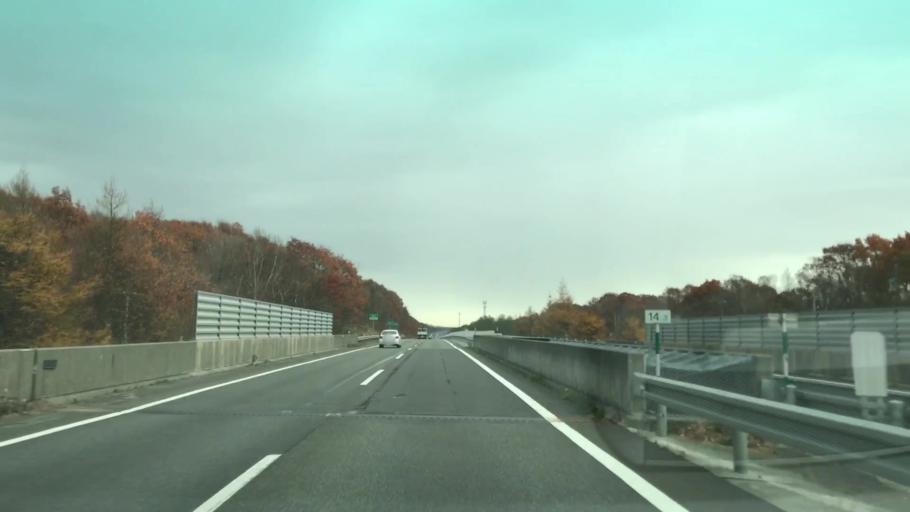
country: JP
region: Hokkaido
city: Tomakomai
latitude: 42.6630
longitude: 141.8106
